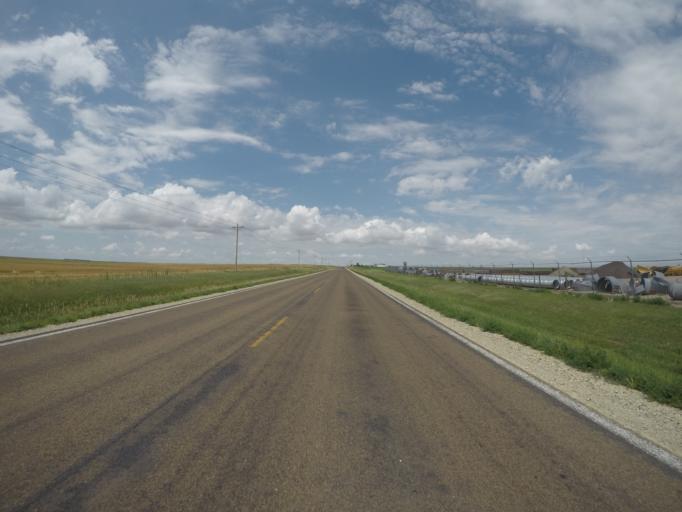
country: US
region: Kansas
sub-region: Rawlins County
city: Atwood
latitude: 39.8387
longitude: -101.0468
